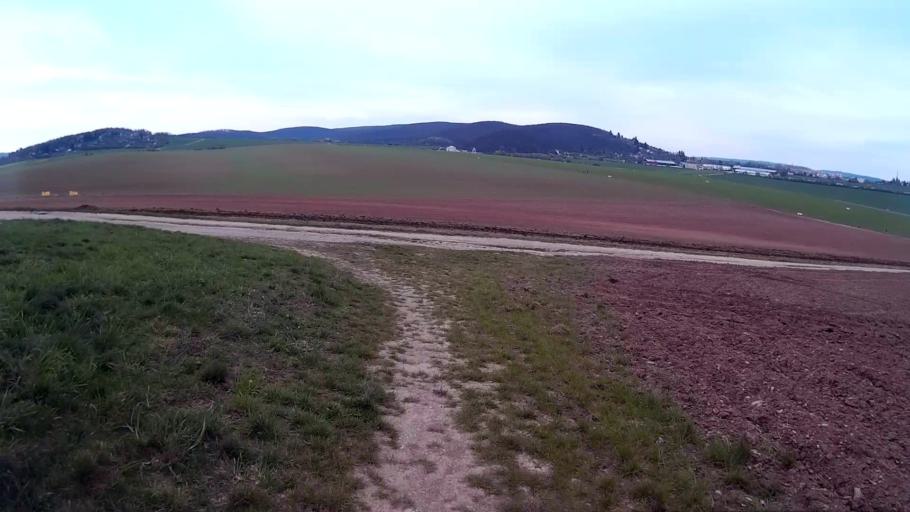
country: CZ
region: South Moravian
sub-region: Mesto Brno
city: Mokra Hora
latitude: 49.2337
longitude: 16.5529
